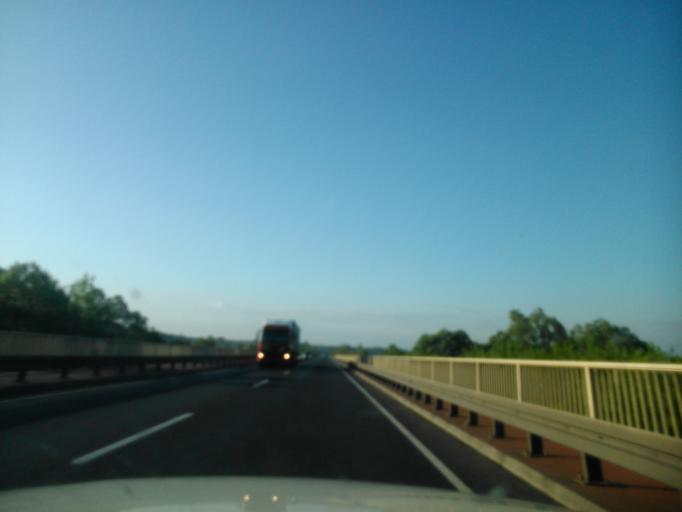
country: PL
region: Masovian Voivodeship
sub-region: Powiat plocki
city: Wyszogrod
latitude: 52.3758
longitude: 20.1880
